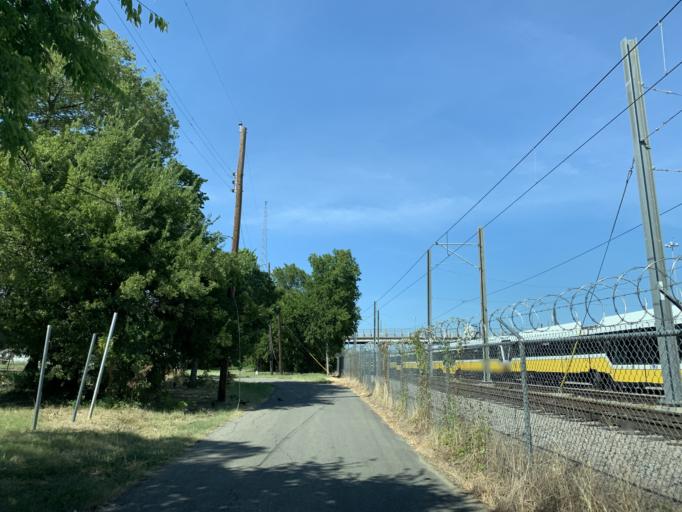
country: US
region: Texas
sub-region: Dallas County
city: Dallas
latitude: 32.7747
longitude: -96.7772
